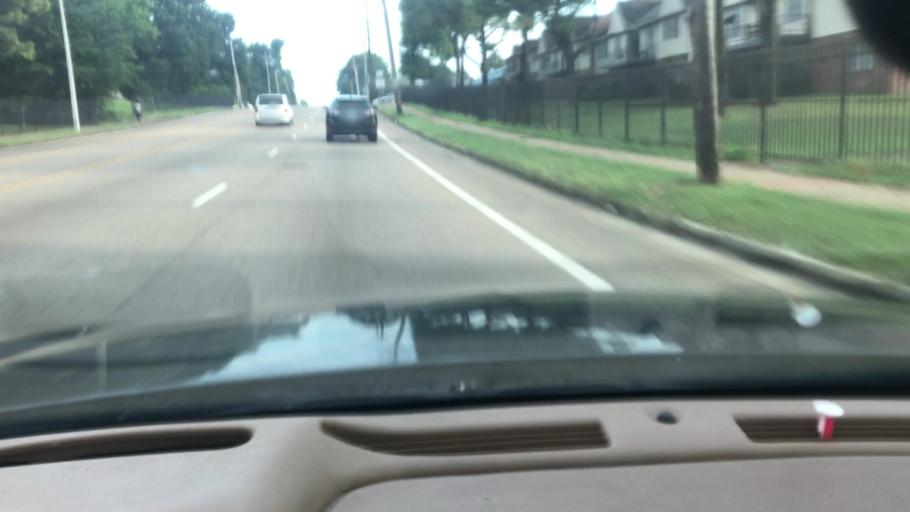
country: US
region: Tennessee
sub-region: Shelby County
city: New South Memphis
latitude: 35.0507
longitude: -90.0076
